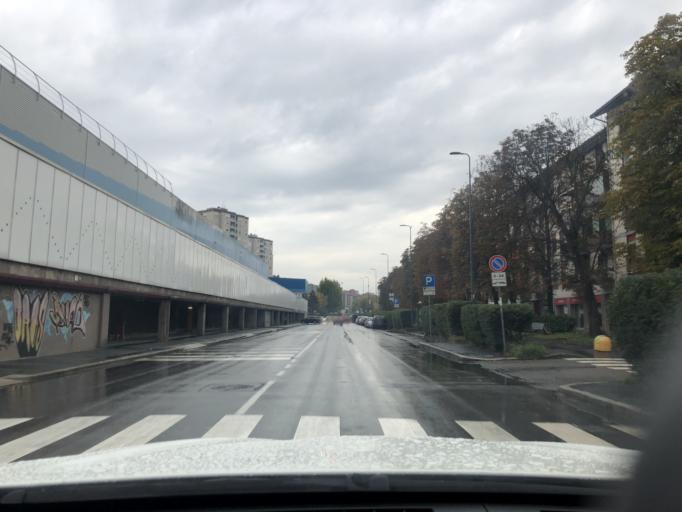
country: IT
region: Lombardy
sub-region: Citta metropolitana di Milano
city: Pero
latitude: 45.4970
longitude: 9.1142
